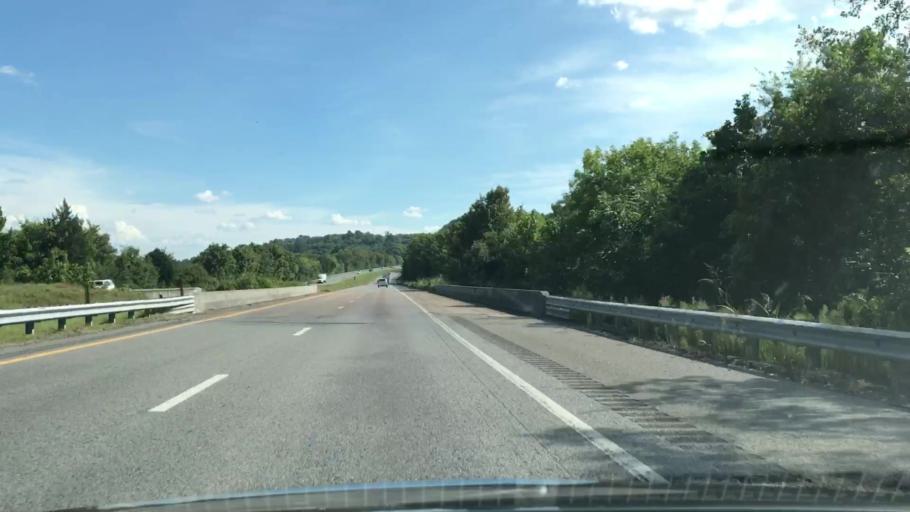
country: US
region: Alabama
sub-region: Limestone County
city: Ardmore
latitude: 35.1309
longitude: -86.8777
